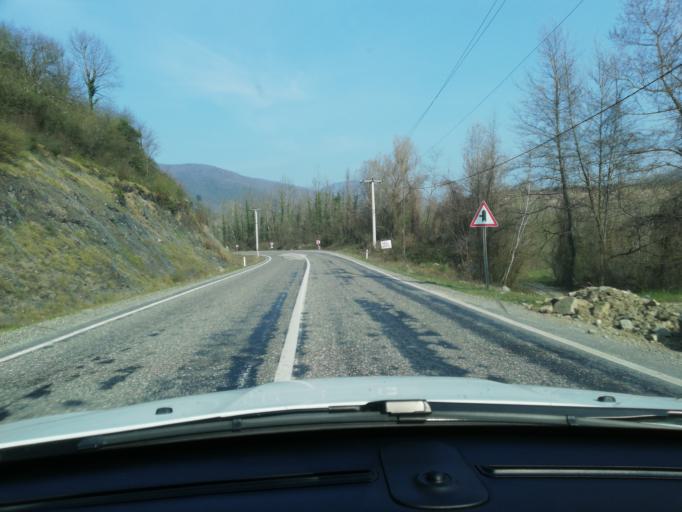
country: TR
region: Karabuk
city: Yenice
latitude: 41.2032
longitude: 32.3718
